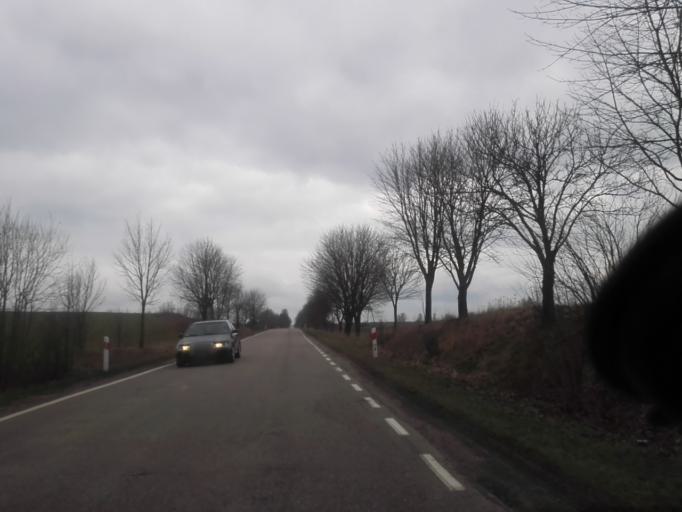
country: PL
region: Podlasie
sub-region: Suwalki
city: Suwalki
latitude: 54.2383
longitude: 22.9153
